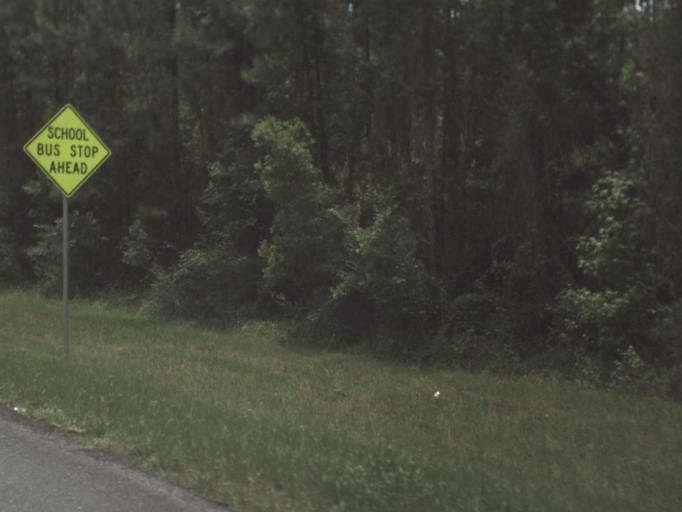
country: US
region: Florida
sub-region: Calhoun County
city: Blountstown
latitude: 30.3866
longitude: -85.0852
